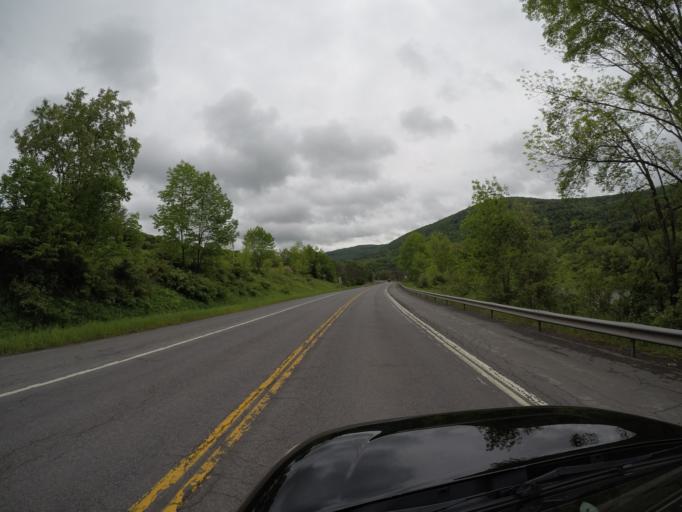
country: US
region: New York
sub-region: Sullivan County
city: Livingston Manor
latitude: 42.1250
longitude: -74.6870
